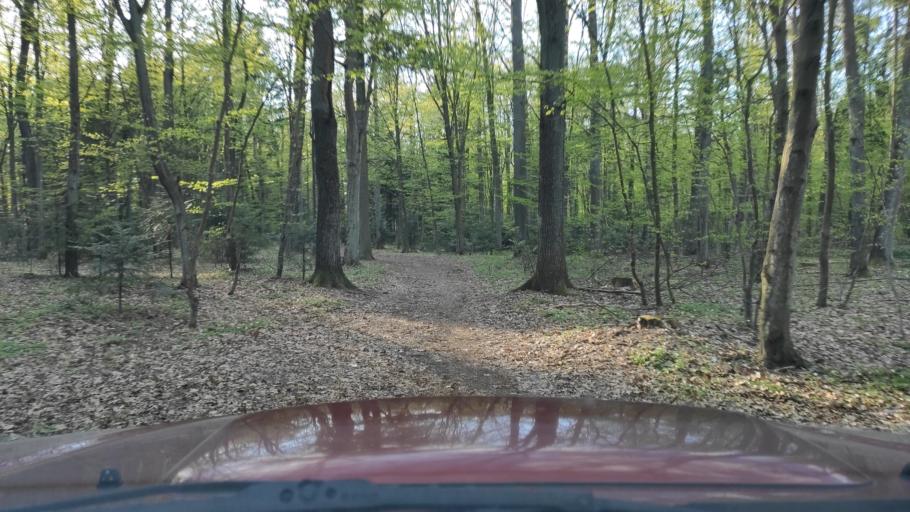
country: PL
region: Masovian Voivodeship
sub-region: Powiat radomski
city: Pionki
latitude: 51.4740
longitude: 21.4362
